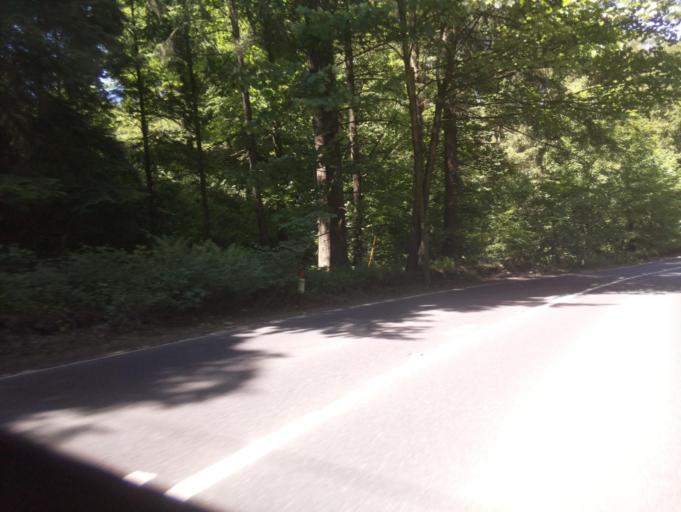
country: GB
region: Scotland
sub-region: Dumfries and Galloway
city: Langholm
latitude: 55.1368
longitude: -2.9898
